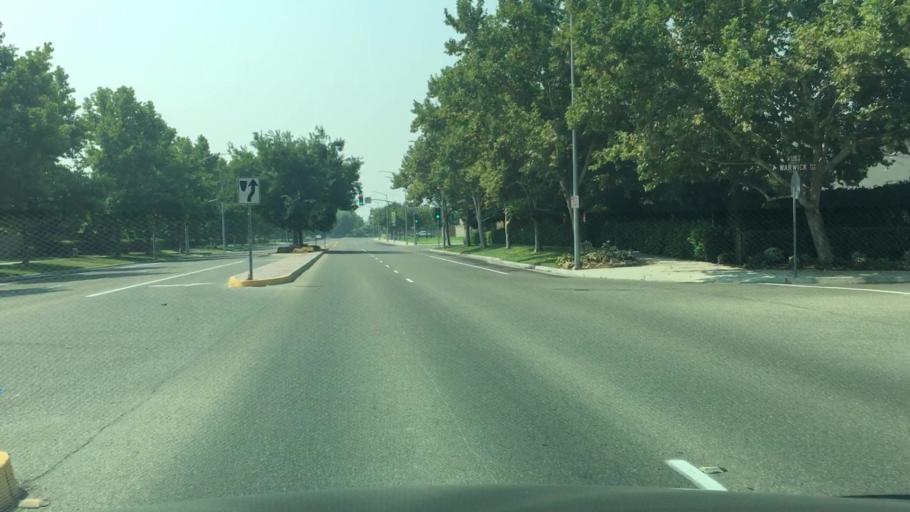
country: US
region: California
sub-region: Fresno County
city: Clovis
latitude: 36.8623
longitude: -119.7022
